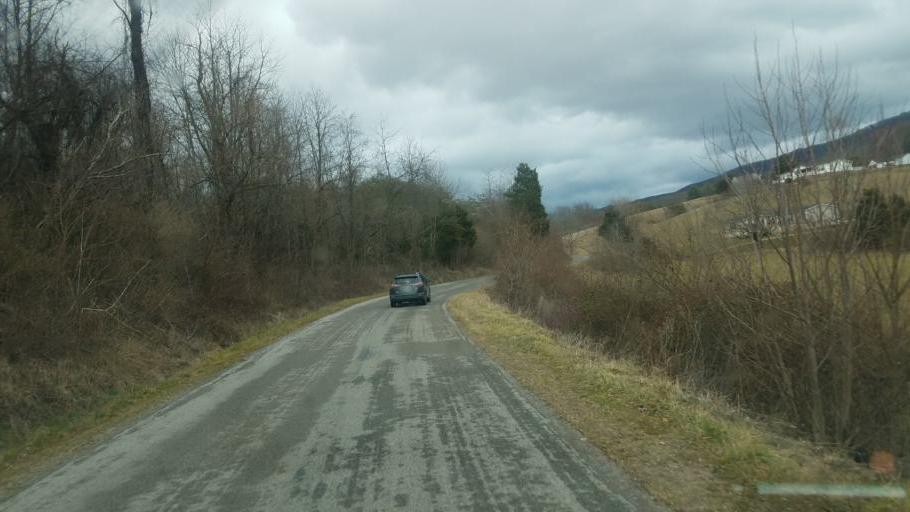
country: US
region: Virginia
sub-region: Giles County
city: Pembroke
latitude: 37.2363
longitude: -80.6880
